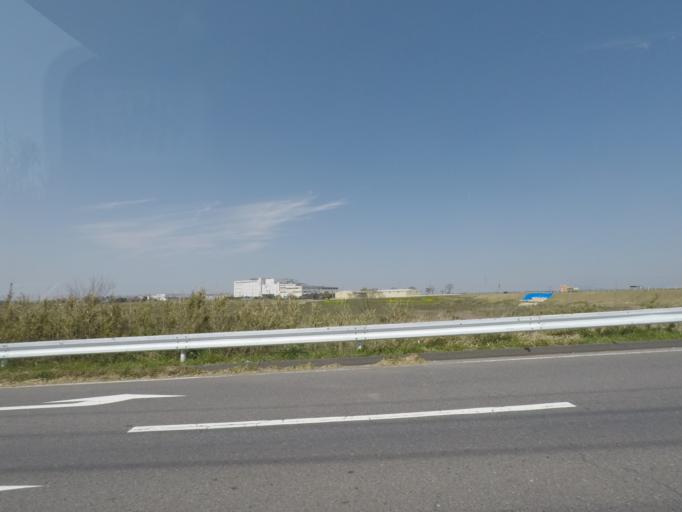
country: JP
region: Ibaraki
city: Edosaki
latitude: 35.8672
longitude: 140.2872
